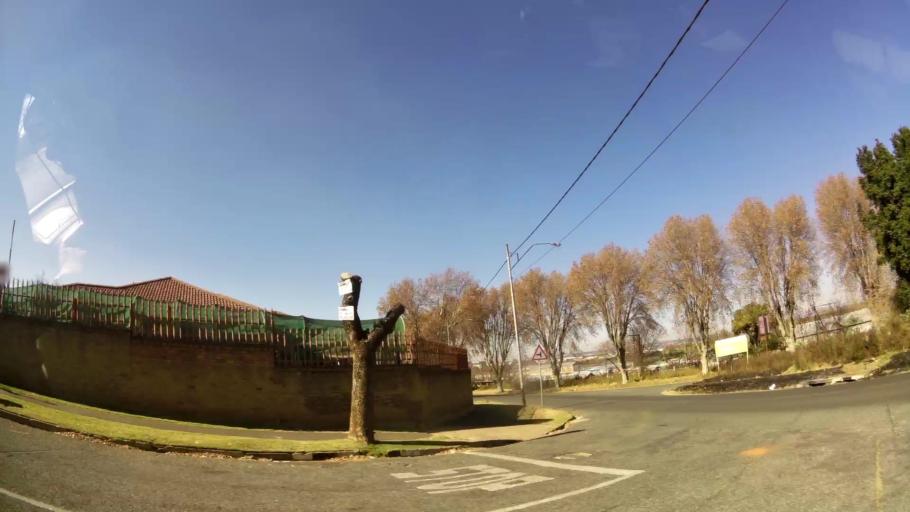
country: ZA
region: Gauteng
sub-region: City of Johannesburg Metropolitan Municipality
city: Johannesburg
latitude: -26.1999
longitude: 27.9898
